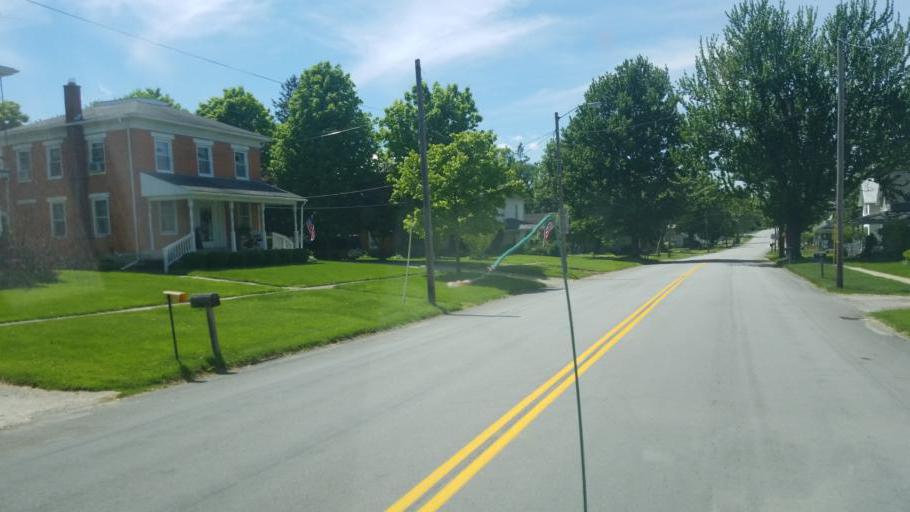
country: US
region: Ohio
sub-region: Huron County
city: Willard
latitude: 41.0651
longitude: -82.8887
